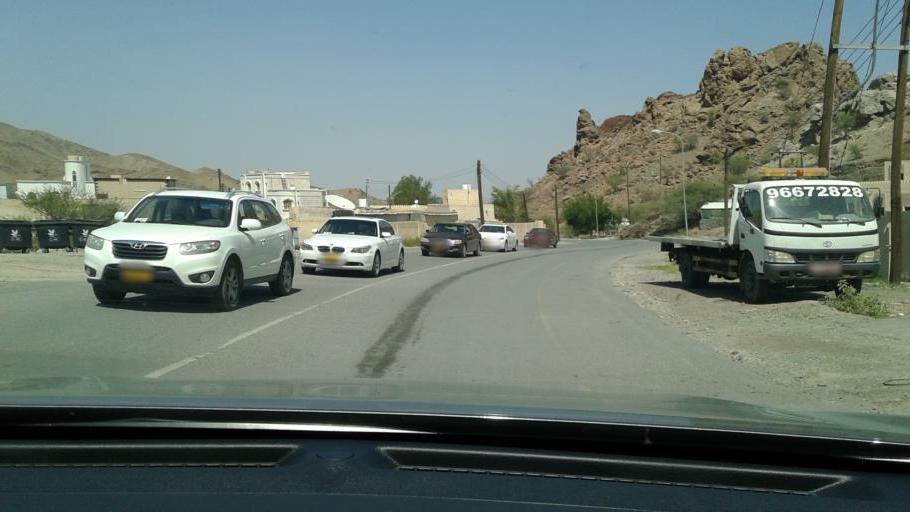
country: OM
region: Al Batinah
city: Rustaq
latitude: 23.3945
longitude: 57.4125
